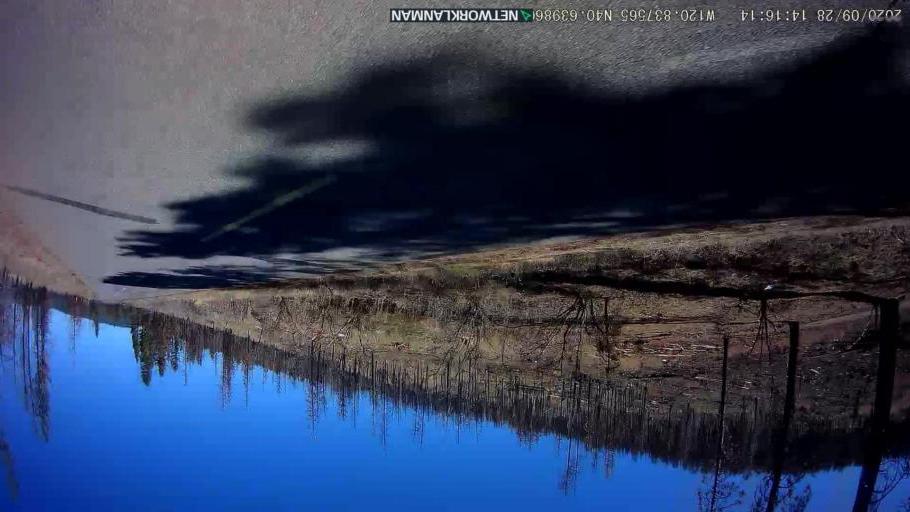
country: US
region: California
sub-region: Lassen County
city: Susanville
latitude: 40.6401
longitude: -120.8375
